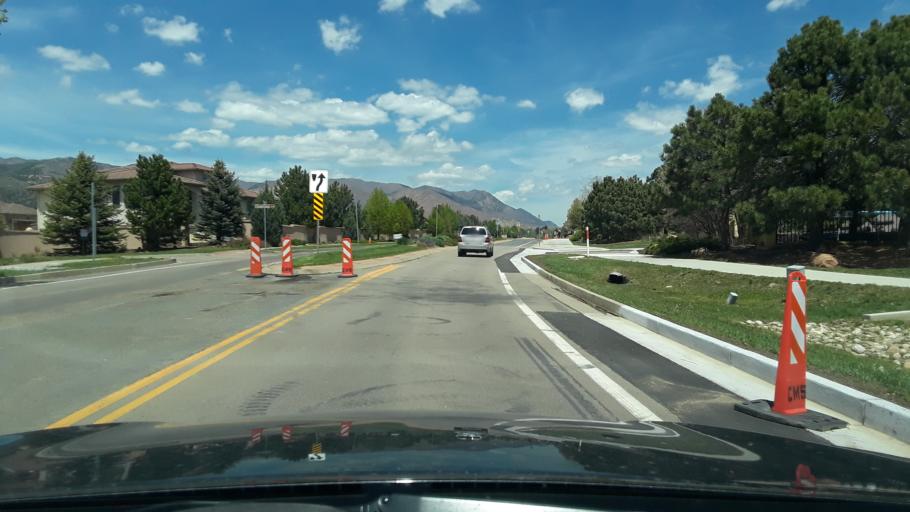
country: US
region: Colorado
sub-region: El Paso County
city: Manitou Springs
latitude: 38.8711
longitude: -104.8634
